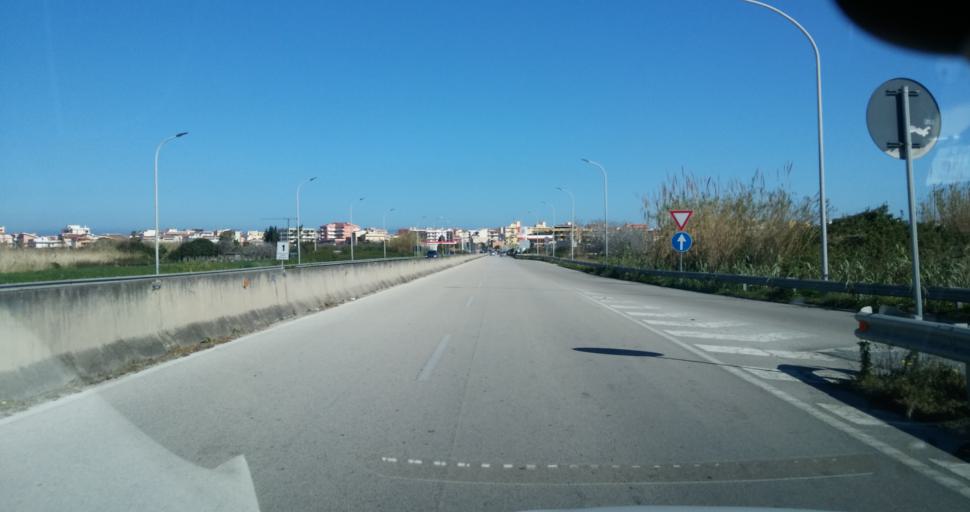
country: IT
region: Sicily
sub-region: Messina
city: Milazzo
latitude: 38.2087
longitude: 15.2378
